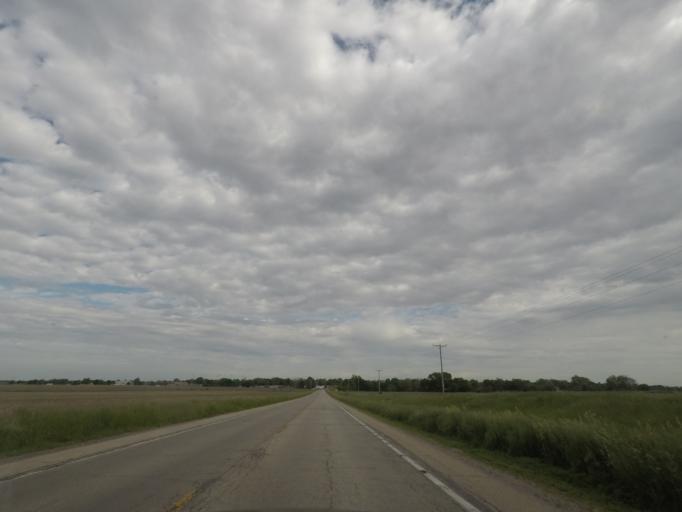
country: US
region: Illinois
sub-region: Logan County
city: Lincoln
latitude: 40.1298
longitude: -89.3437
